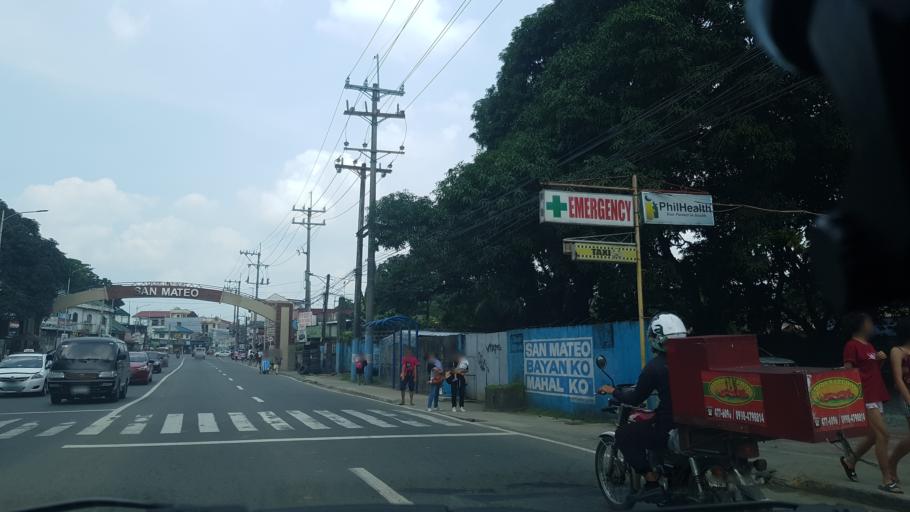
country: PH
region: Calabarzon
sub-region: Province of Rizal
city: San Mateo
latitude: 14.6737
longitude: 121.1096
